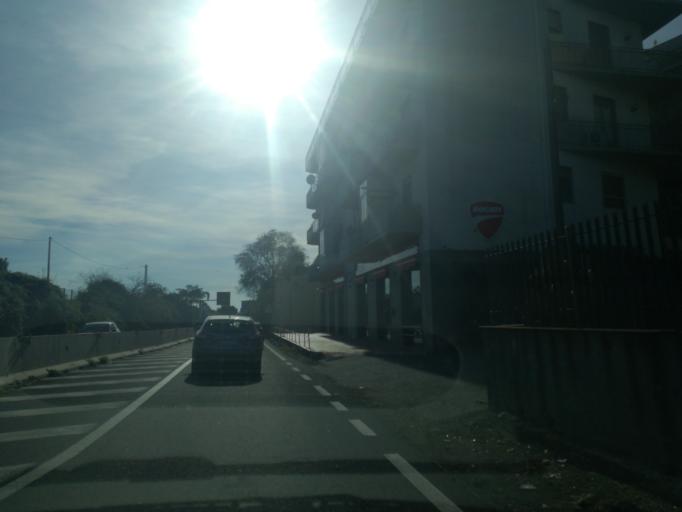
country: IT
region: Sicily
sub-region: Catania
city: Acireale
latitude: 37.6029
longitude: 15.1687
